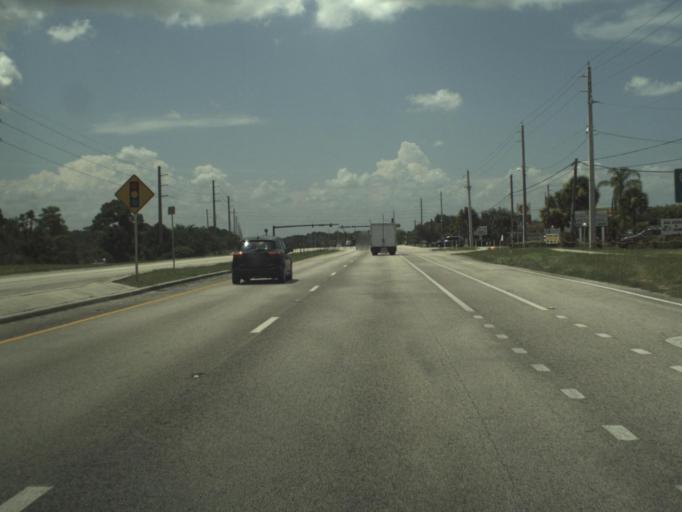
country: US
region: Florida
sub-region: Martin County
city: Hobe Sound
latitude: 27.0966
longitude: -80.1574
